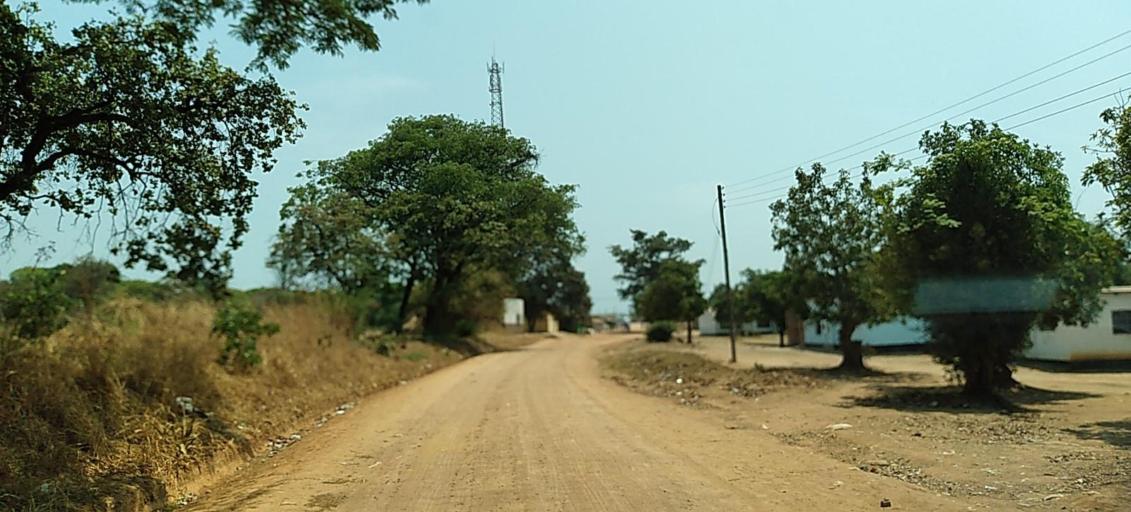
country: ZM
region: Copperbelt
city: Chingola
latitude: -12.5987
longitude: 27.9561
